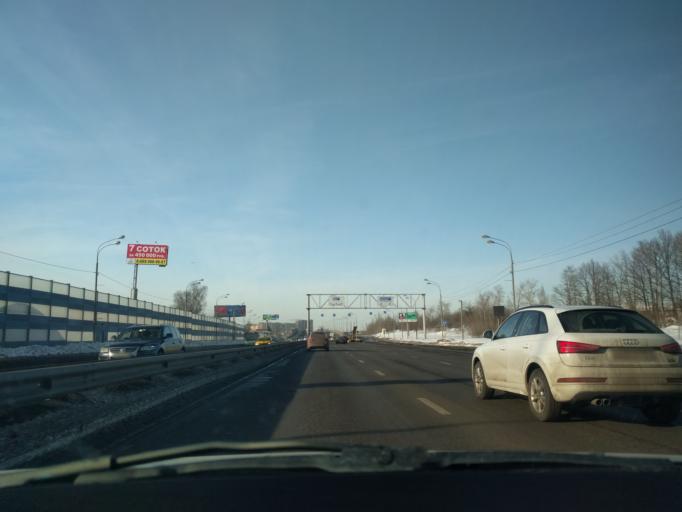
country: RU
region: Moscow
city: Severnyy
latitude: 55.9442
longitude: 37.5430
